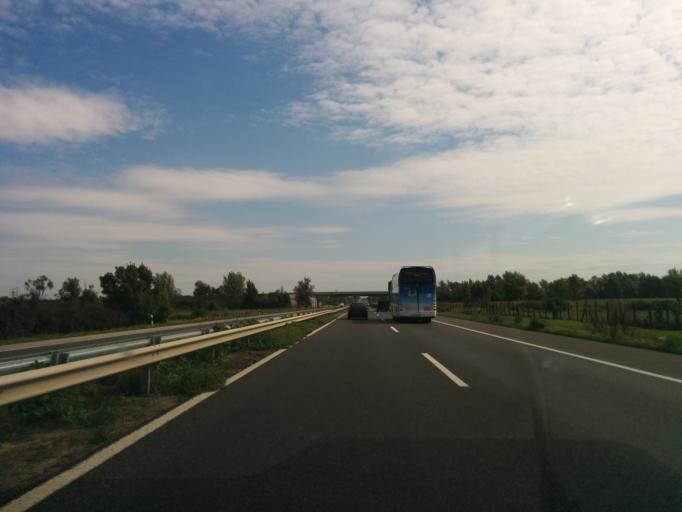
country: HU
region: Gyor-Moson-Sopron
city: Toltestava
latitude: 47.6394
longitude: 17.6897
